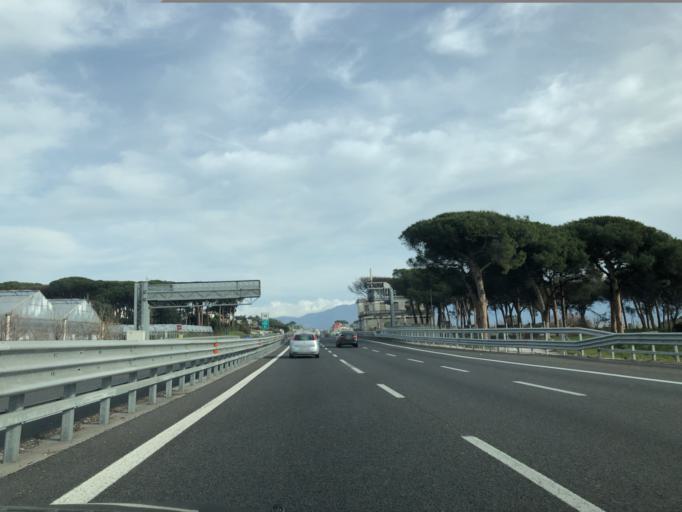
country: IT
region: Campania
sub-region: Provincia di Napoli
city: Torre del Greco
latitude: 40.7759
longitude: 14.4035
